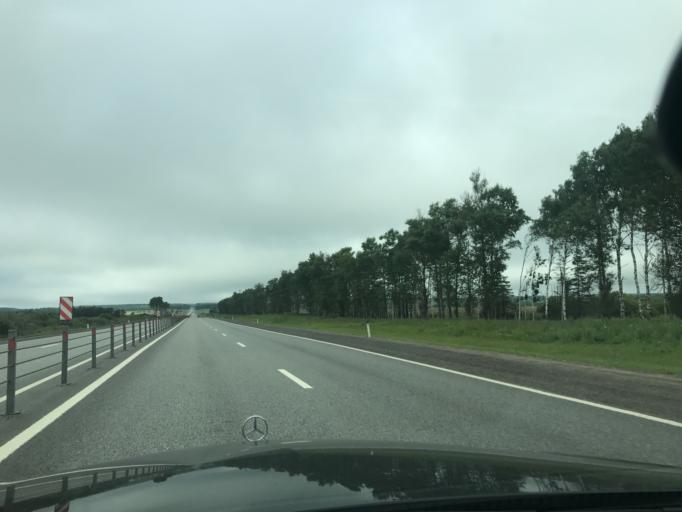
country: RU
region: Smolensk
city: Vyaz'ma
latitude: 55.3469
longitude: 34.6162
